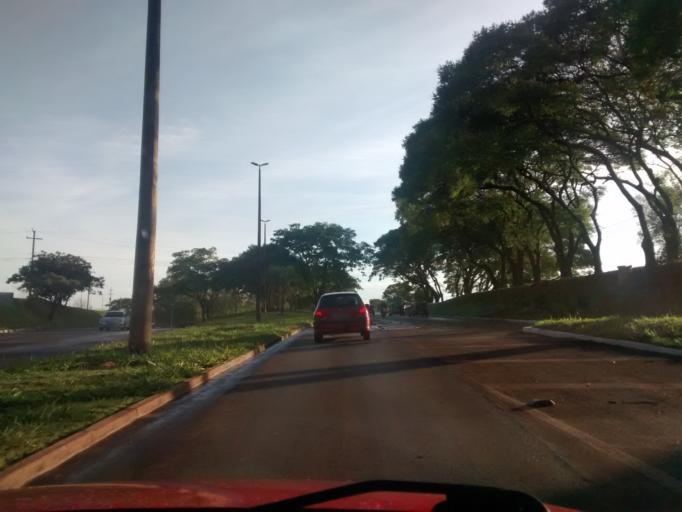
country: BR
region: Federal District
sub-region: Brasilia
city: Brasilia
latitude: -15.7835
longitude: -47.8734
